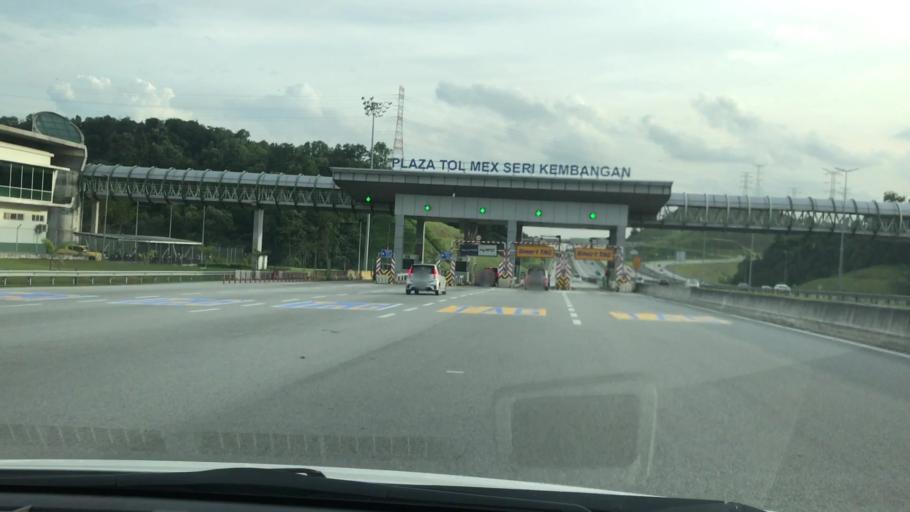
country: MY
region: Selangor
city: Kampong Baharu Balakong
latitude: 3.0178
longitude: 101.6838
